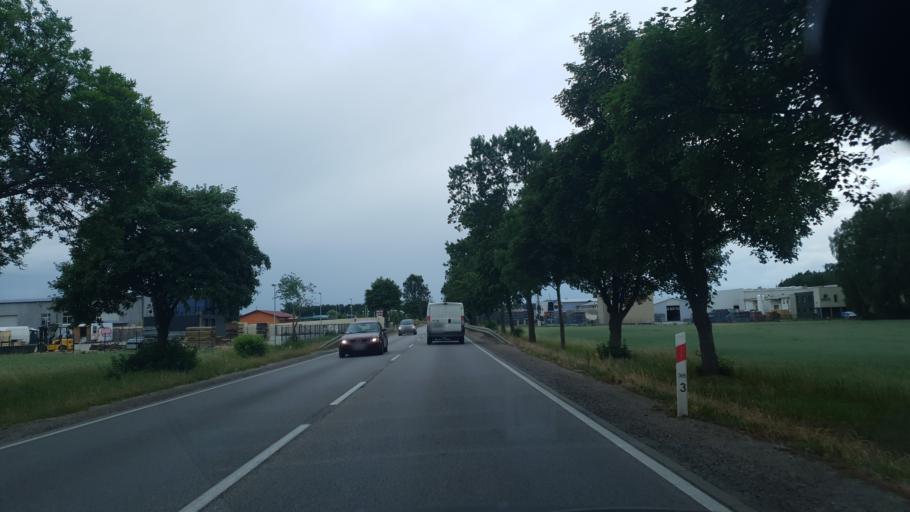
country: PL
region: Pomeranian Voivodeship
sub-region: Powiat kartuski
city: Banino
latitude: 54.4070
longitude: 18.3668
